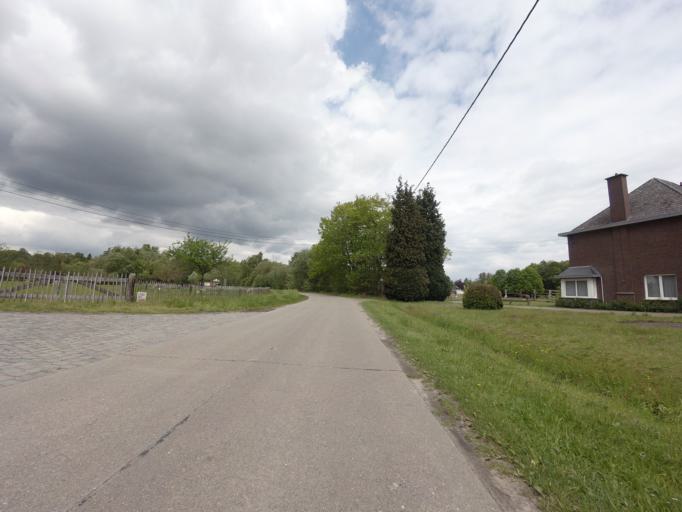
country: BE
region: Flanders
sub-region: Provincie Antwerpen
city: Mechelen
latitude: 51.0655
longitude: 4.4698
